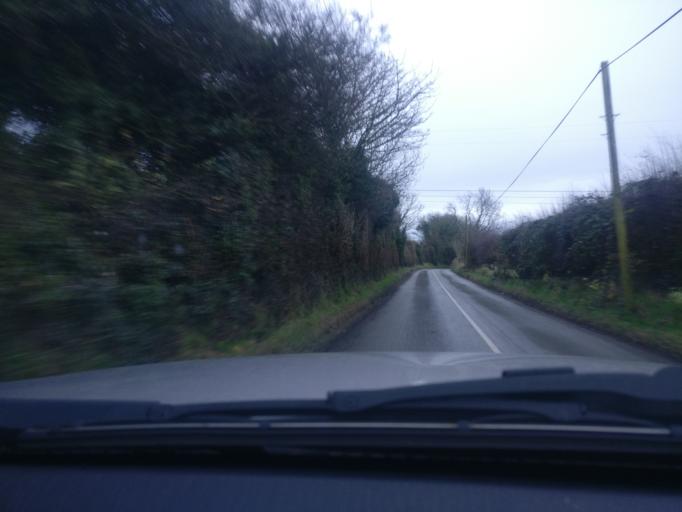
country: IE
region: Leinster
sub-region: Kildare
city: Kilcock
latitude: 53.4721
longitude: -6.6252
